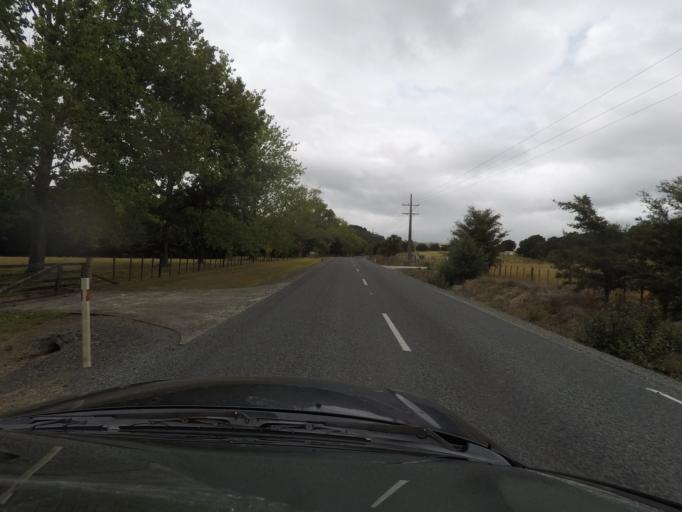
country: NZ
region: Auckland
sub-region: Auckland
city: Wellsford
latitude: -36.2804
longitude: 174.5944
